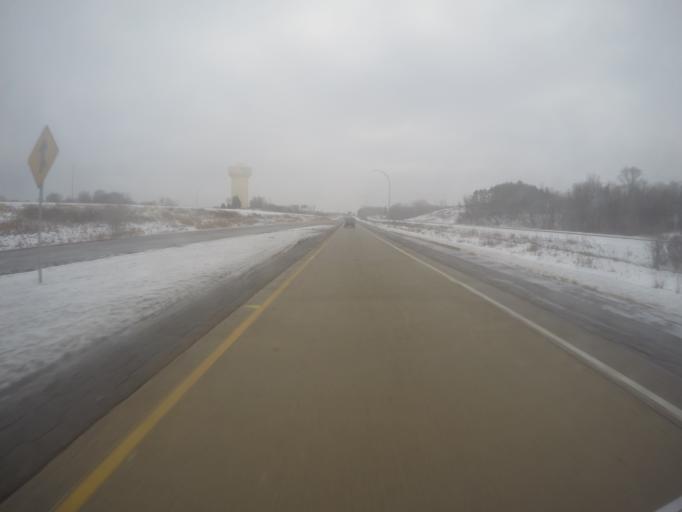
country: US
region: Minnesota
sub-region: Dakota County
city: Inver Grove Heights
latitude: 44.8254
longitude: -93.0616
